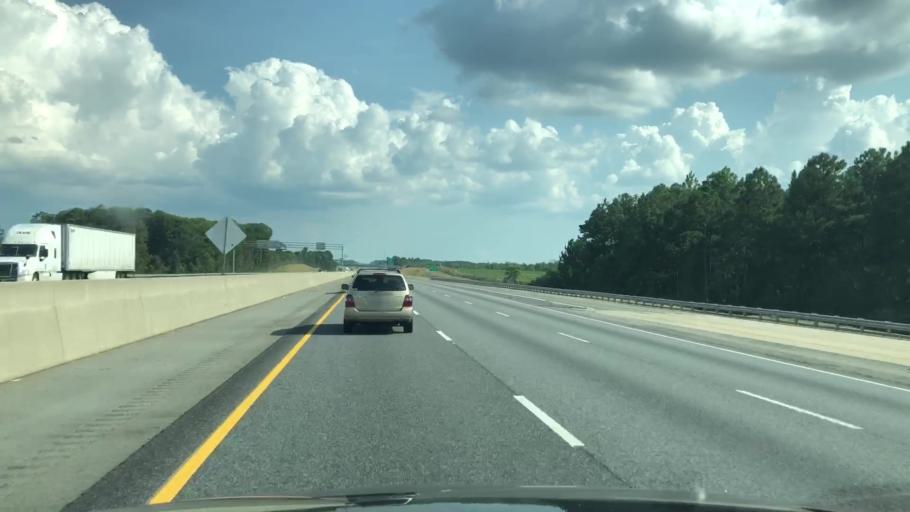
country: US
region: Georgia
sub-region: Turner County
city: Ashburn
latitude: 31.6788
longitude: -83.6193
